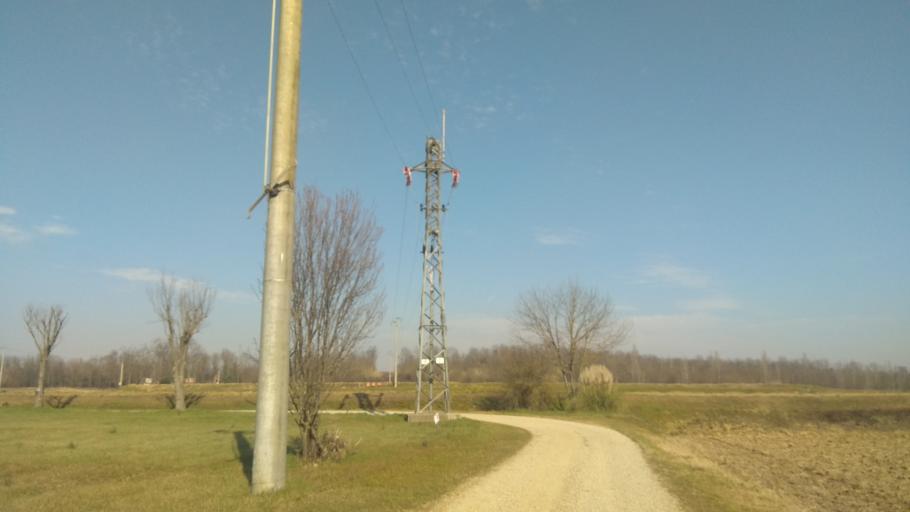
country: IT
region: Piedmont
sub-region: Provincia di Vercelli
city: Palazzolo Vercellese
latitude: 45.2164
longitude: 8.2309
